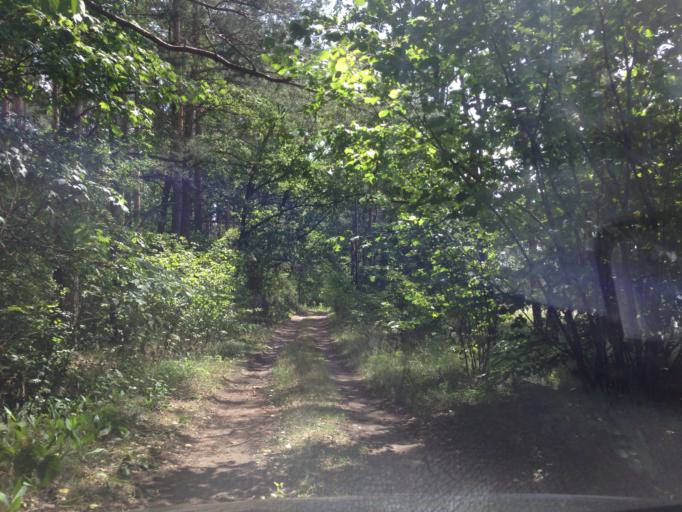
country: PL
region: Kujawsko-Pomorskie
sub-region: Powiat brodnicki
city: Bartniczka
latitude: 53.2827
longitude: 19.5650
